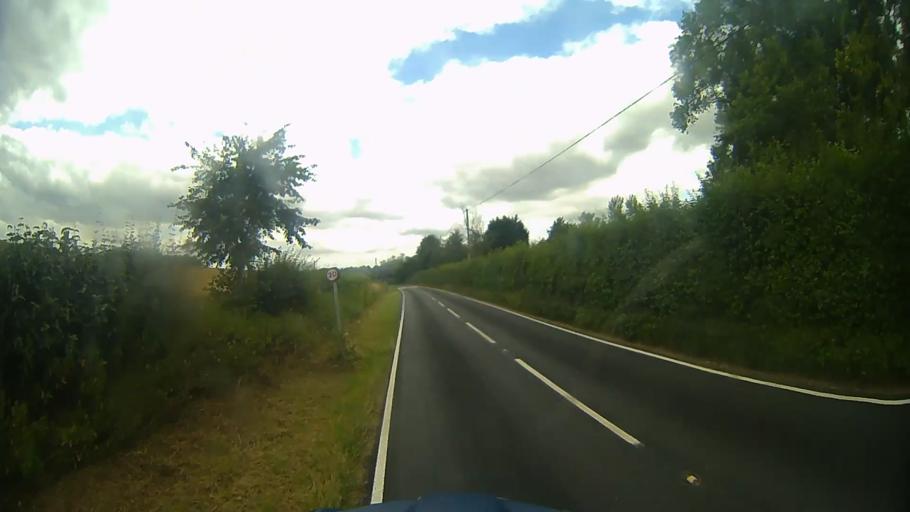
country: GB
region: England
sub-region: Hampshire
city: Four Marks
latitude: 51.1072
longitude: -1.1602
